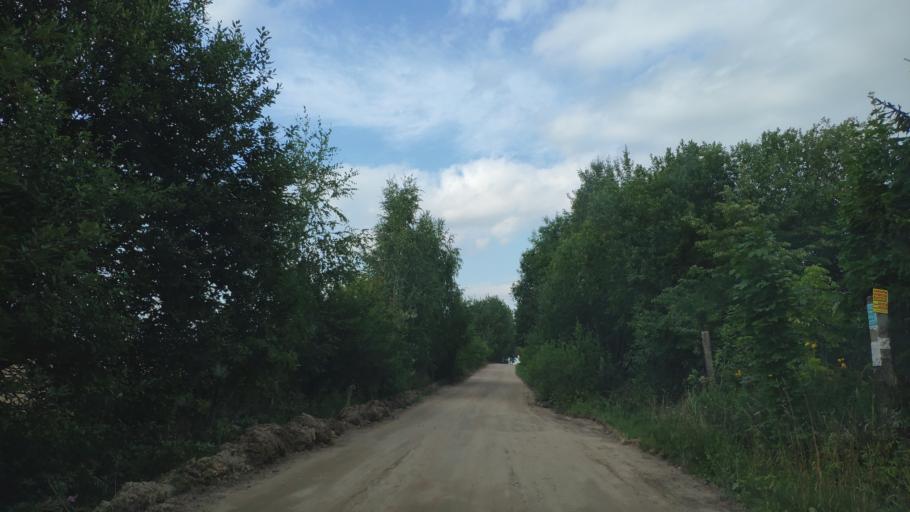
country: BY
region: Minsk
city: Khatsyezhyna
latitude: 53.8501
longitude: 27.2887
